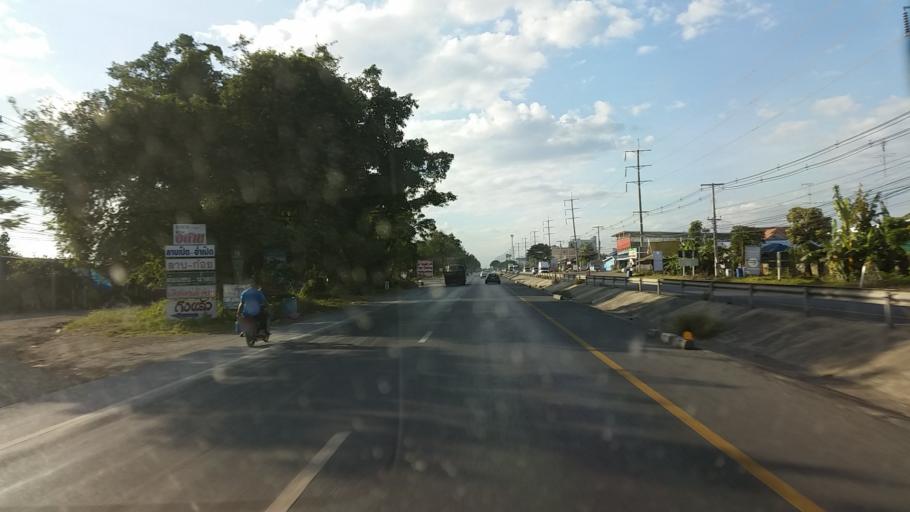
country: TH
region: Lop Buri
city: Phatthana Nikhom
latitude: 14.8282
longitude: 100.9108
